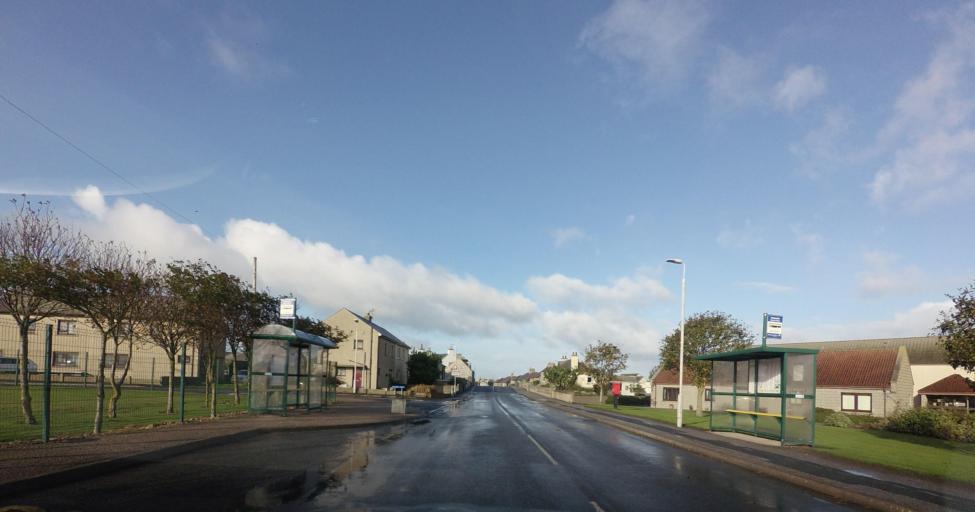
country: GB
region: Scotland
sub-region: Aberdeenshire
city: Whitehills
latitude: 57.6761
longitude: -2.5750
